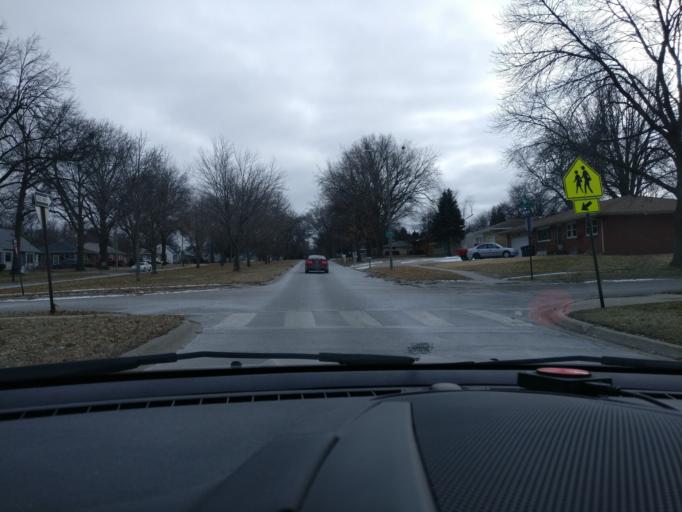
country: US
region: Nebraska
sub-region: Lancaster County
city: Lincoln
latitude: 40.8457
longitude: -96.6402
